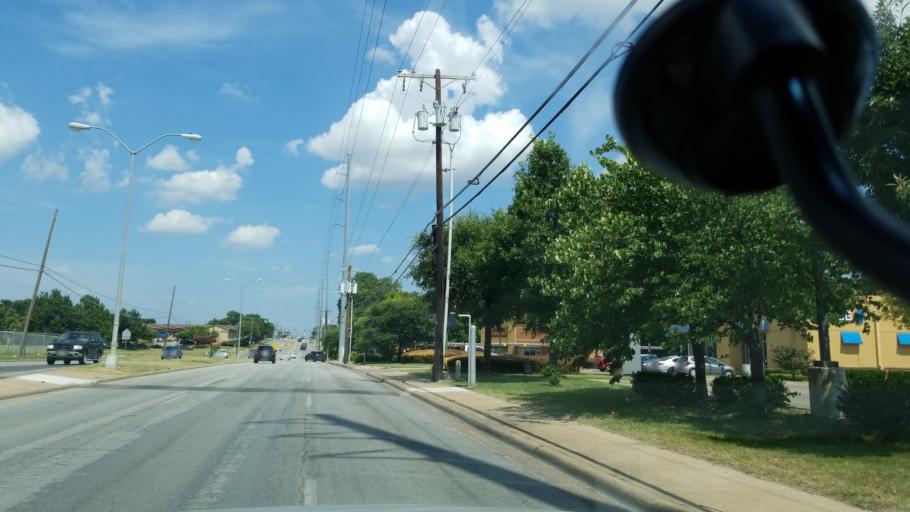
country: US
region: Texas
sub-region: Dallas County
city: Cockrell Hill
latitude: 32.7203
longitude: -96.8816
